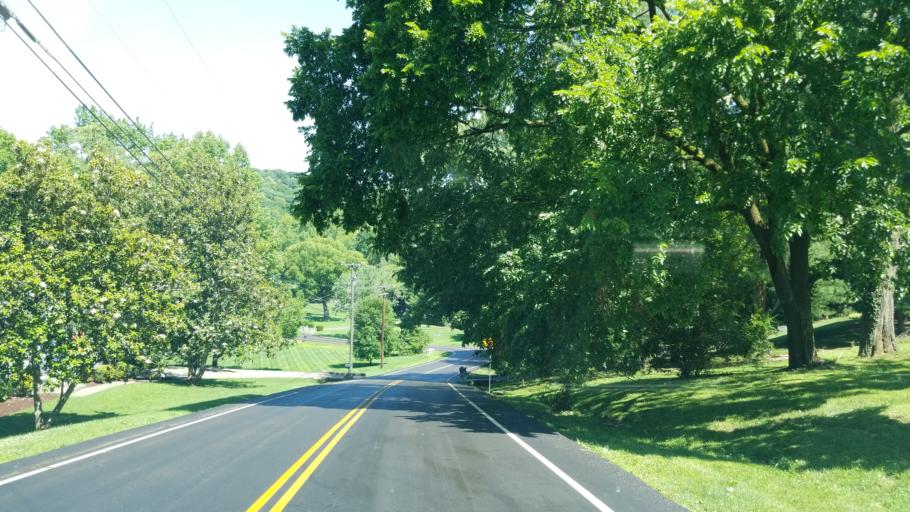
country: US
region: Tennessee
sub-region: Davidson County
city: Forest Hills
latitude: 36.0612
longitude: -86.8200
